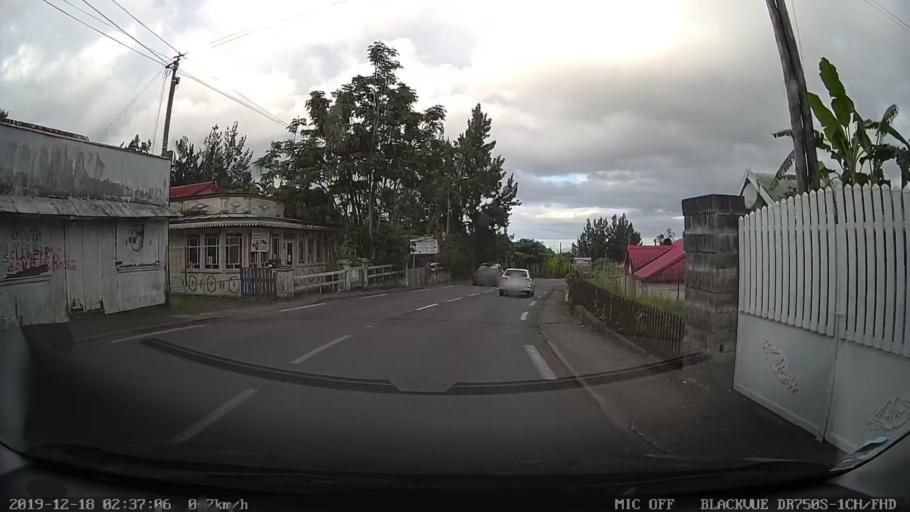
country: RE
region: Reunion
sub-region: Reunion
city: Saint-Benoit
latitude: -21.1389
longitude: 55.6232
